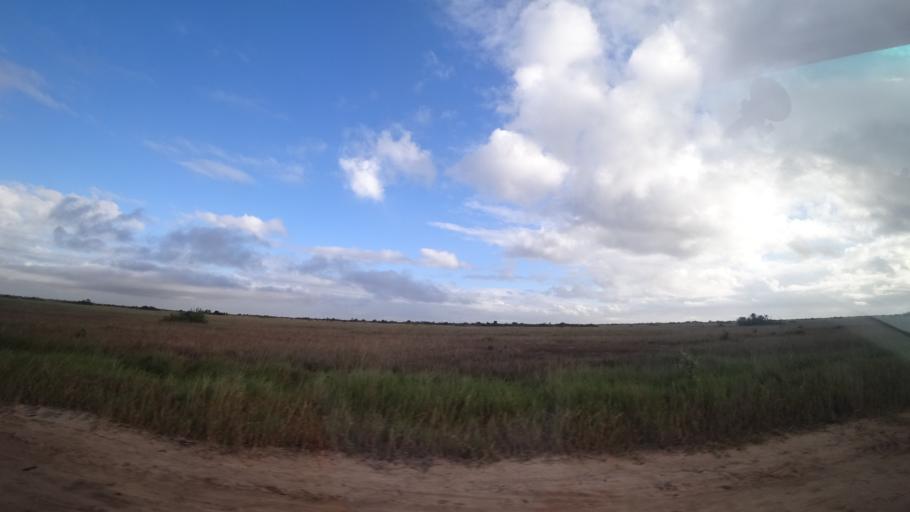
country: MZ
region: Sofala
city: Beira
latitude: -19.7013
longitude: 35.0257
